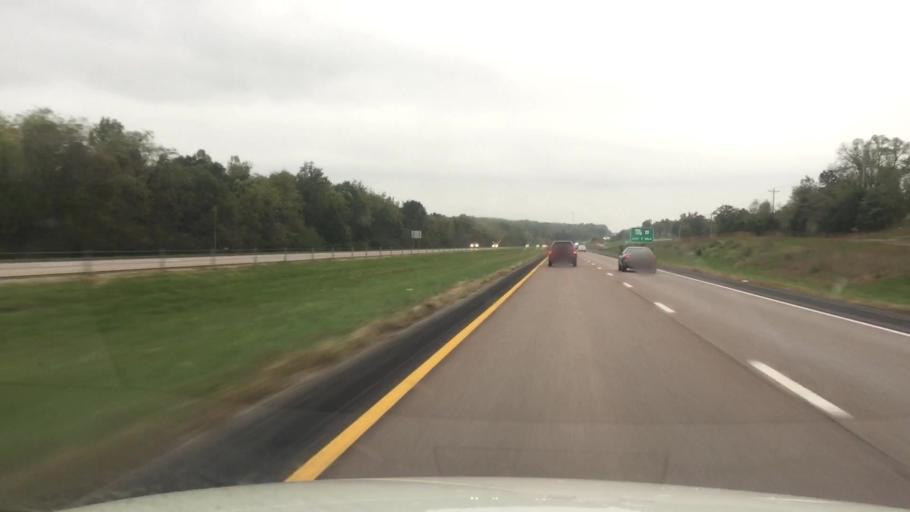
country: US
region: Missouri
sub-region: Boone County
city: Ashland
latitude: 38.8133
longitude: -92.2513
